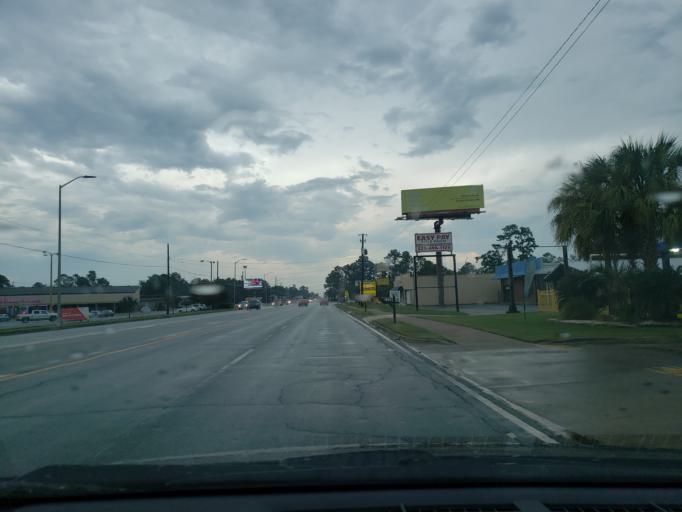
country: US
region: Georgia
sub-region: Dougherty County
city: Albany
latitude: 31.6081
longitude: -84.1759
